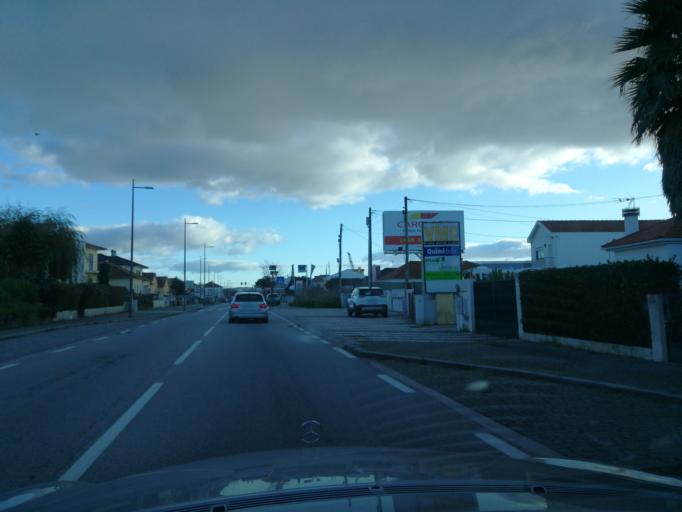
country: PT
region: Viana do Castelo
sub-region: Viana do Castelo
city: Viana do Castelo
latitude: 41.6998
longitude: -8.8463
